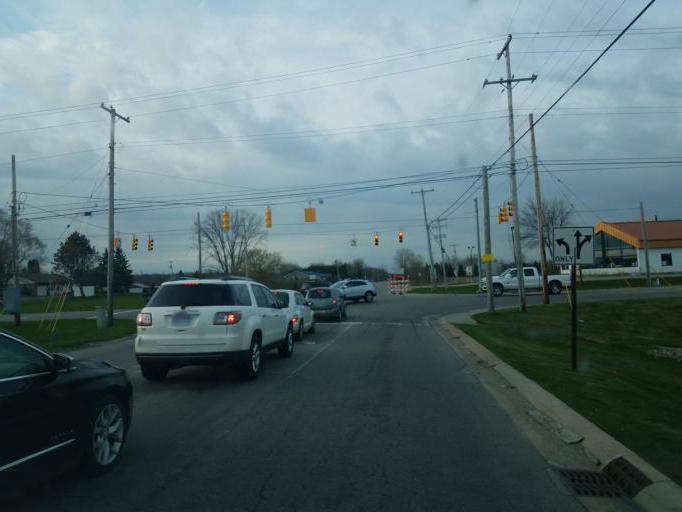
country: US
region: Michigan
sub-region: Isabella County
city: Mount Pleasant
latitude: 43.5981
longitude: -84.8087
